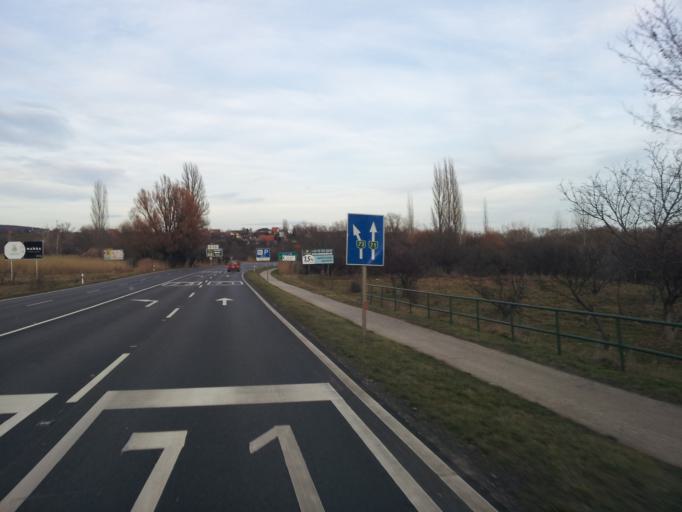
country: HU
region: Veszprem
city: Csopak
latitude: 46.9712
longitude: 17.9138
